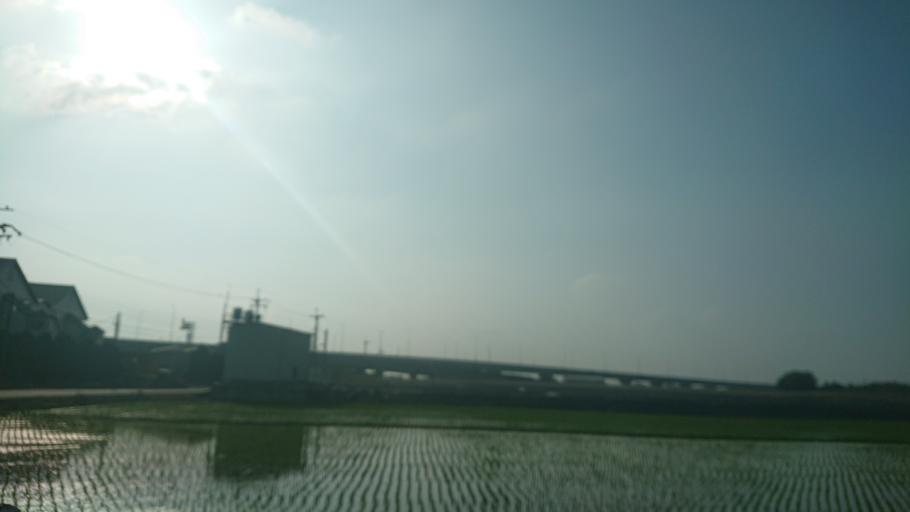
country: TW
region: Taiwan
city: Xinying
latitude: 23.1963
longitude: 120.2717
